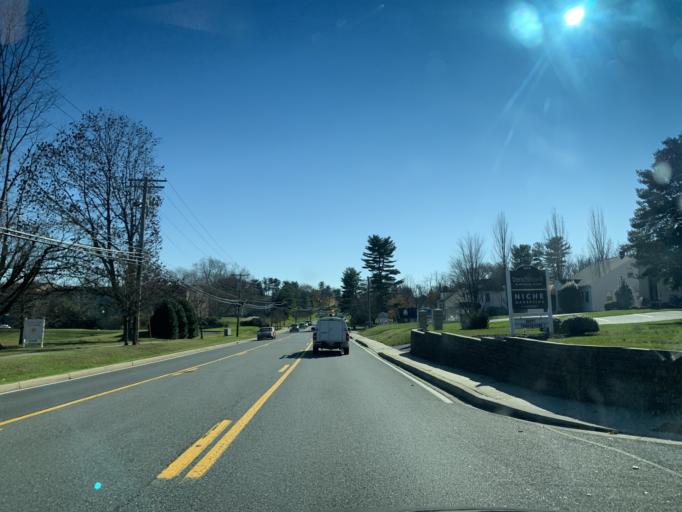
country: US
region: Maryland
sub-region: Harford County
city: South Bel Air
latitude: 39.5307
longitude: -76.3432
